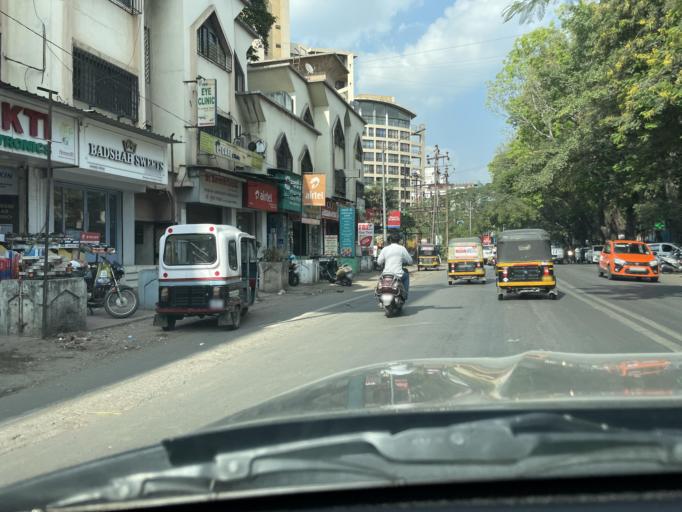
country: IN
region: Maharashtra
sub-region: Pune Division
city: Pune
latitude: 18.5014
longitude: 73.9005
